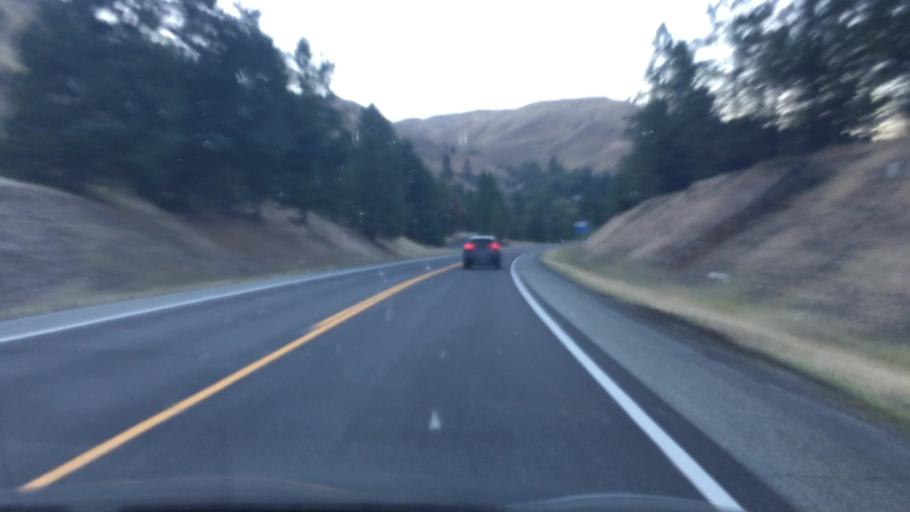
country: US
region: Idaho
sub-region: Valley County
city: McCall
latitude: 45.3028
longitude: -116.3620
